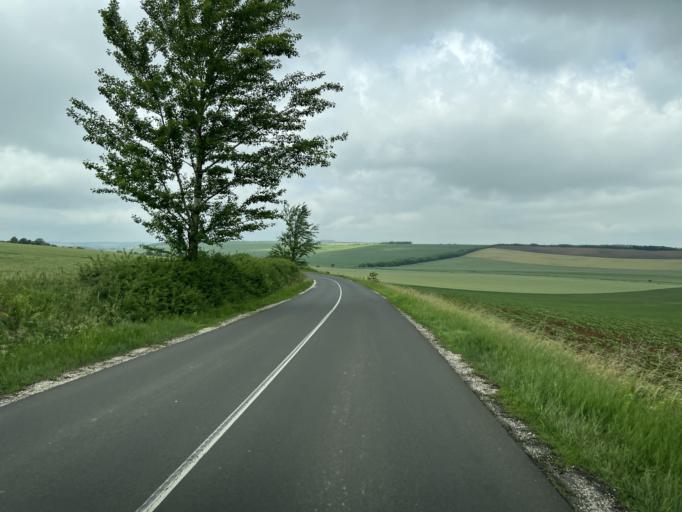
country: HU
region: Pest
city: Kartal
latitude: 47.7267
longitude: 19.5336
